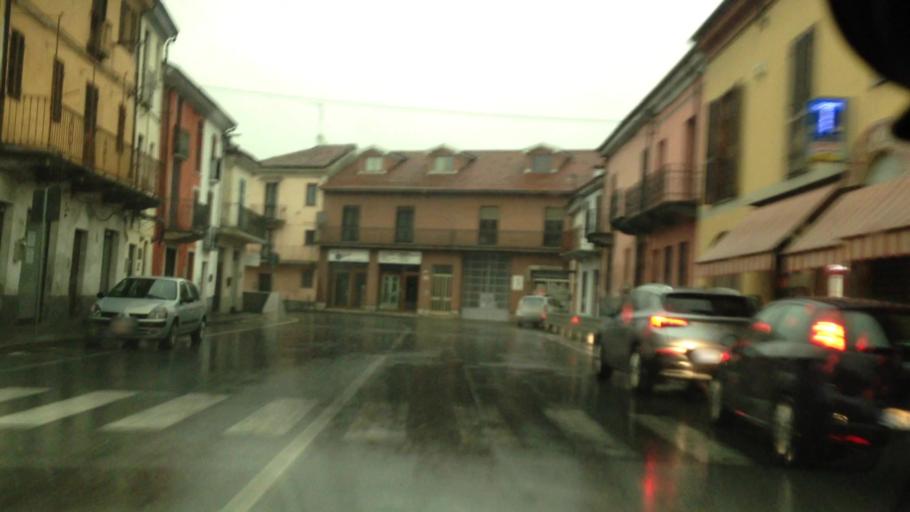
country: IT
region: Piedmont
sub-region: Provincia di Asti
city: Castello di Annone
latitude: 44.8794
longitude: 8.3139
